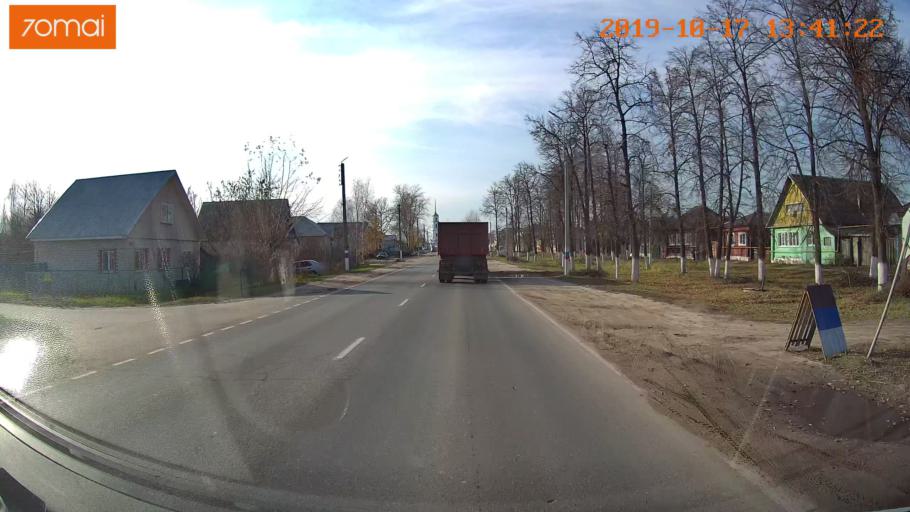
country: RU
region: Rjazan
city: Tuma
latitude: 55.1490
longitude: 40.5655
